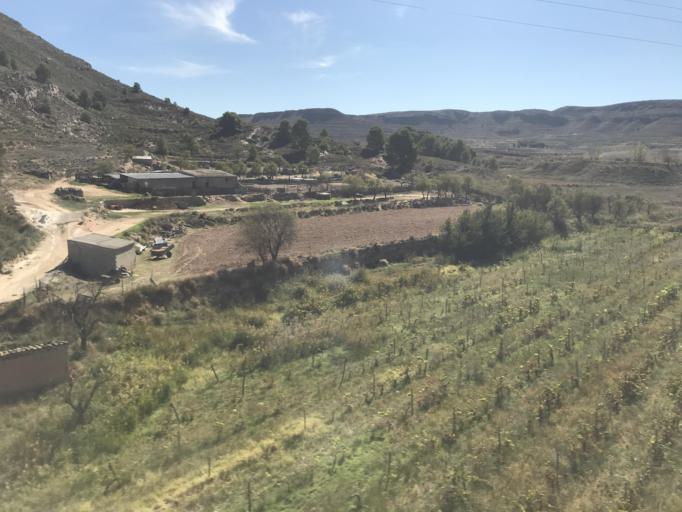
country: ES
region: Aragon
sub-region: Provincia de Zaragoza
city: Alhama de Aragon
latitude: 41.2950
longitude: -1.8765
